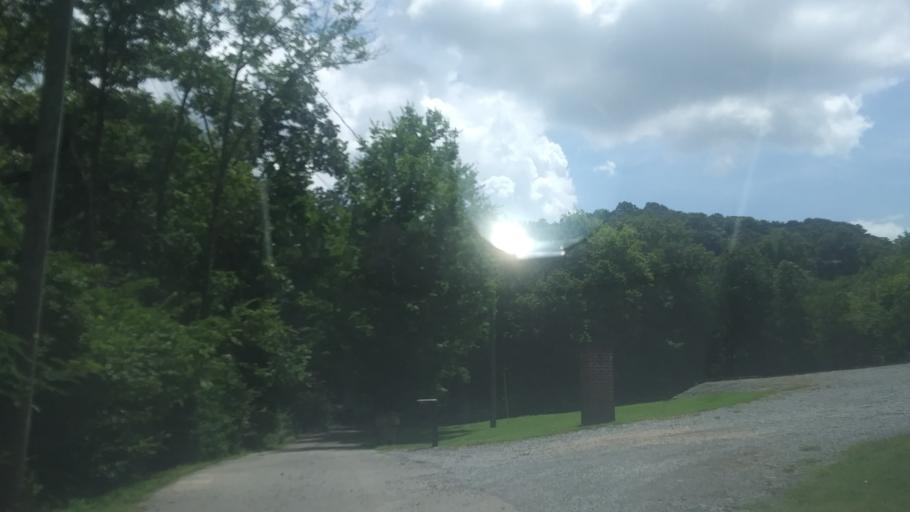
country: US
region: Tennessee
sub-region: Davidson County
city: Belle Meade
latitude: 36.1145
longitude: -86.9204
